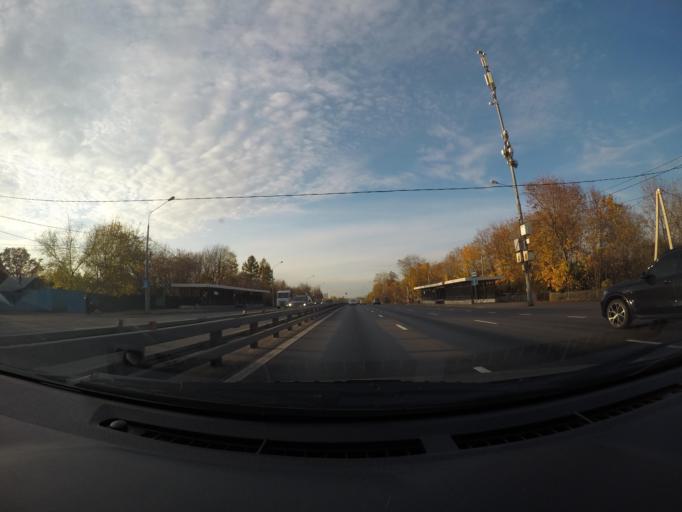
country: RU
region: Moskovskaya
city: Novopodrezkovo
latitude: 55.9256
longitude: 37.3859
